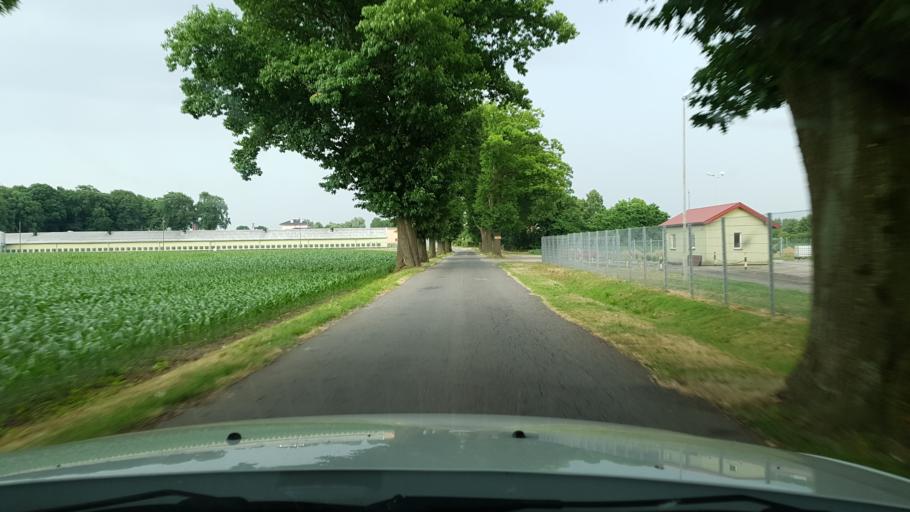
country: PL
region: West Pomeranian Voivodeship
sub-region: Powiat lobeski
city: Lobez
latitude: 53.6767
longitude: 15.6756
